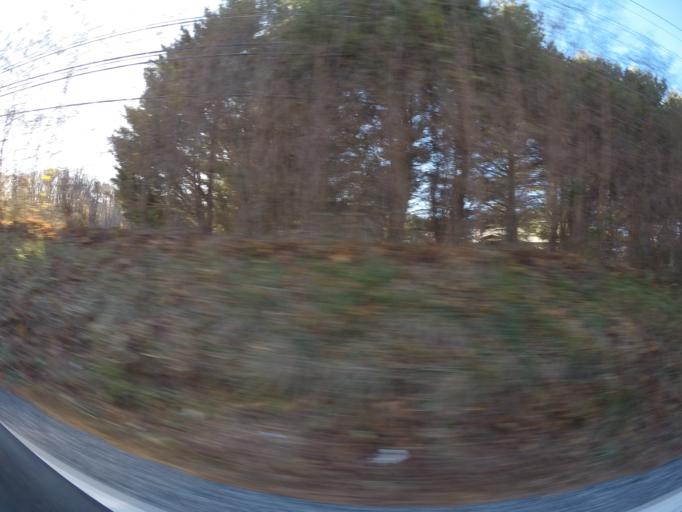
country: US
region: Maryland
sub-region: Harford County
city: South Bel Air
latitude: 39.5669
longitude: -76.2537
